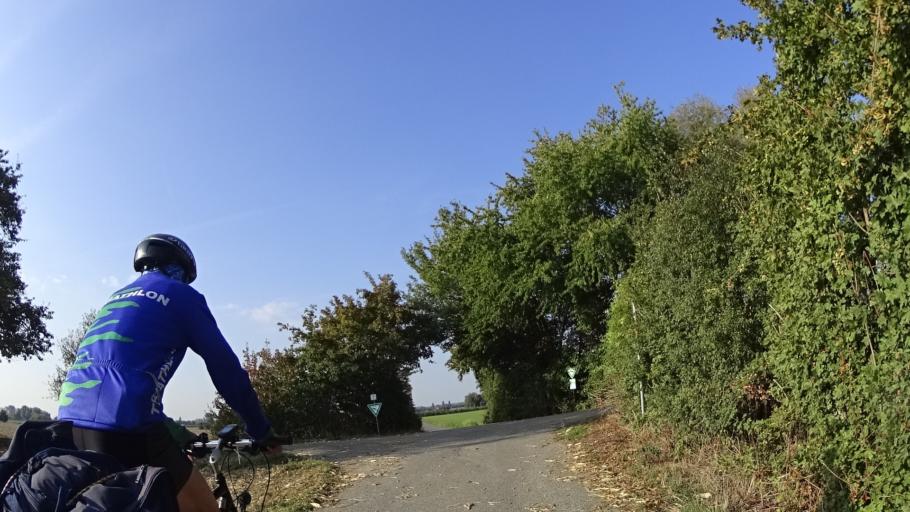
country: DE
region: Baden-Wuerttemberg
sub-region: Karlsruhe Region
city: Ketsch
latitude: 49.3459
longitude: 8.4979
